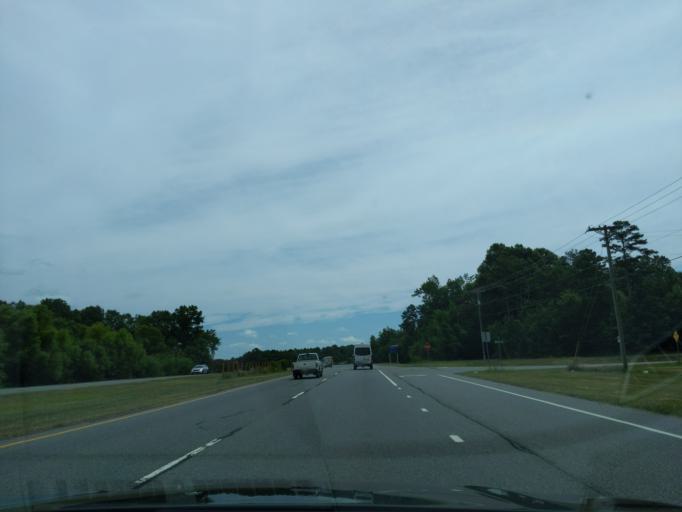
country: US
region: North Carolina
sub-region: Cabarrus County
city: Mount Pleasant
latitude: 35.3860
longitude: -80.5026
